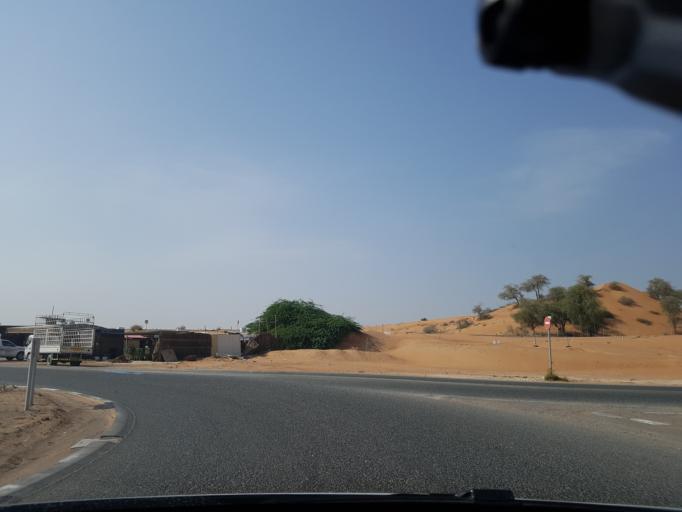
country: AE
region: Umm al Qaywayn
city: Umm al Qaywayn
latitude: 25.5286
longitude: 55.7233
